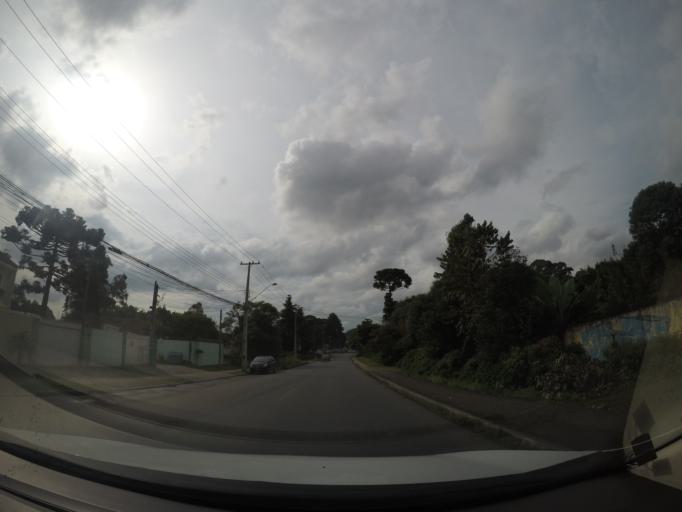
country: BR
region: Parana
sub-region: Sao Jose Dos Pinhais
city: Sao Jose dos Pinhais
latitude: -25.5159
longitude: -49.2611
